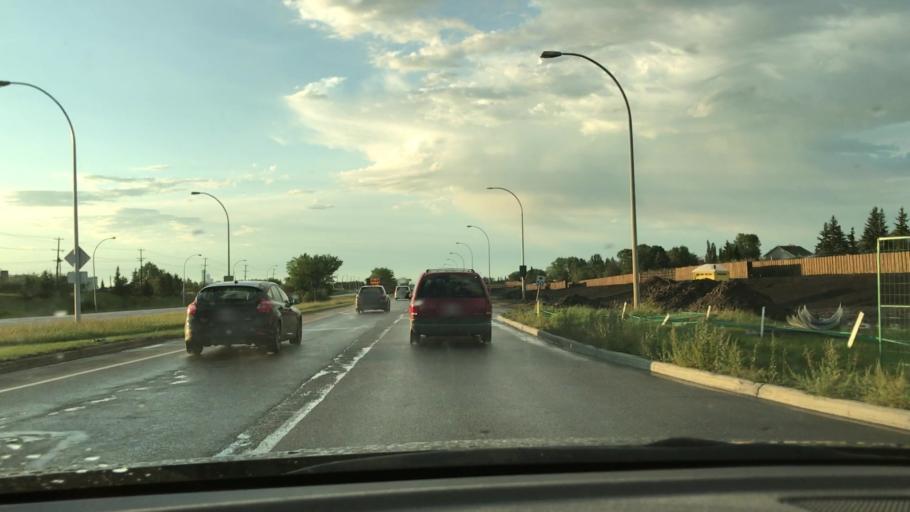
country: CA
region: Alberta
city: Edmonton
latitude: 53.4744
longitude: -113.4663
